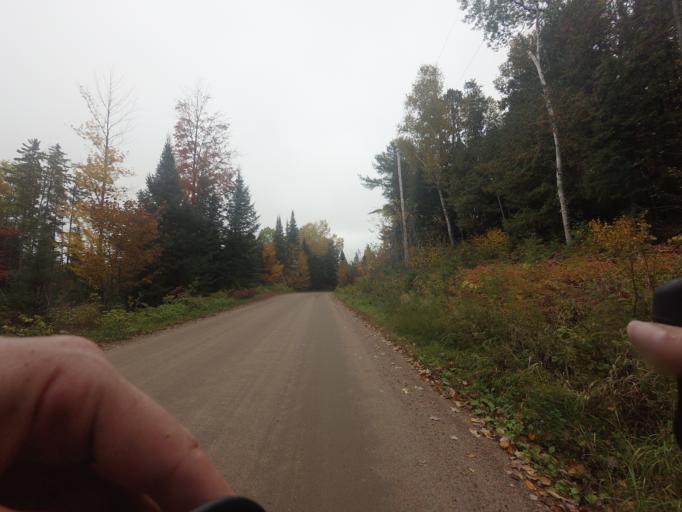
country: CA
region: Ontario
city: Pembroke
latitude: 45.7482
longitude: -77.2276
